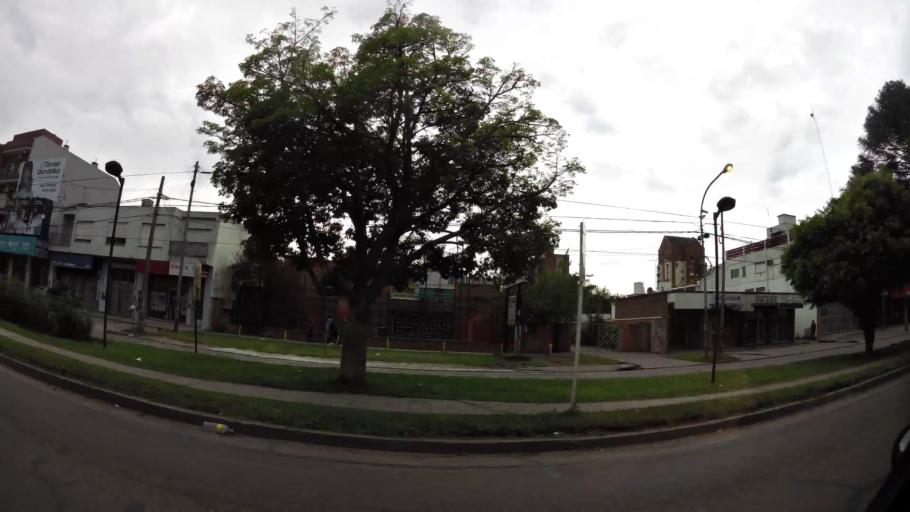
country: AR
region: Buenos Aires
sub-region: Partido de Quilmes
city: Quilmes
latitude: -34.8017
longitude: -58.2784
